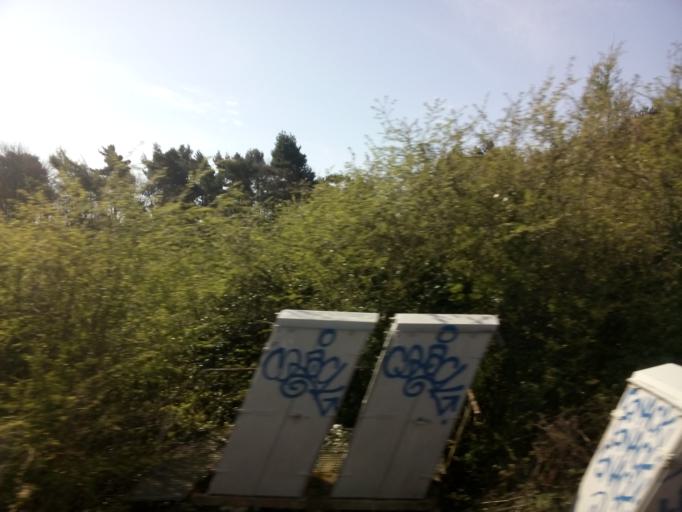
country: GB
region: Scotland
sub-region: East Lothian
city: Musselburgh
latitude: 55.9288
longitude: -3.0544
